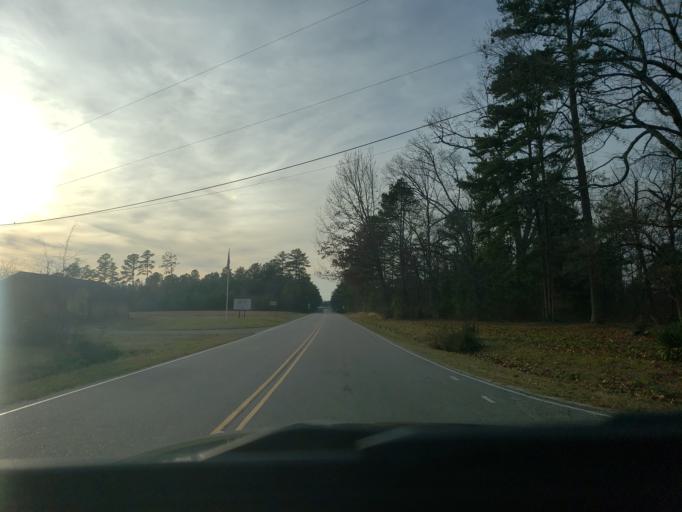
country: US
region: North Carolina
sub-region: Cleveland County
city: Boiling Springs
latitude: 35.3050
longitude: -81.7085
